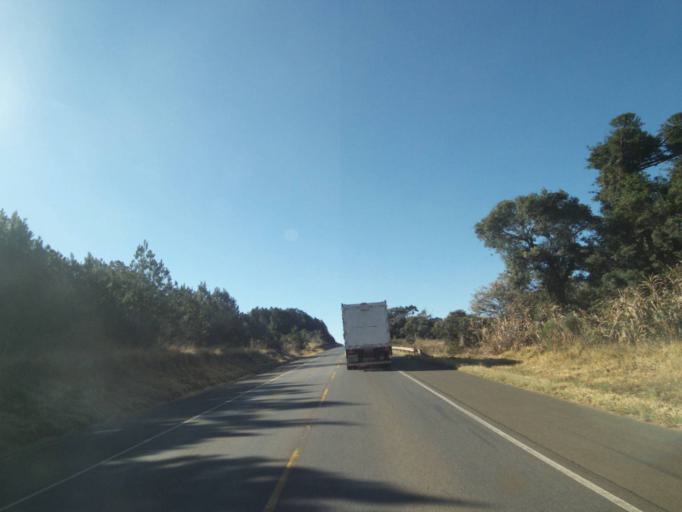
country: BR
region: Parana
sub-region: Tibagi
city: Tibagi
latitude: -24.5466
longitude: -50.4512
